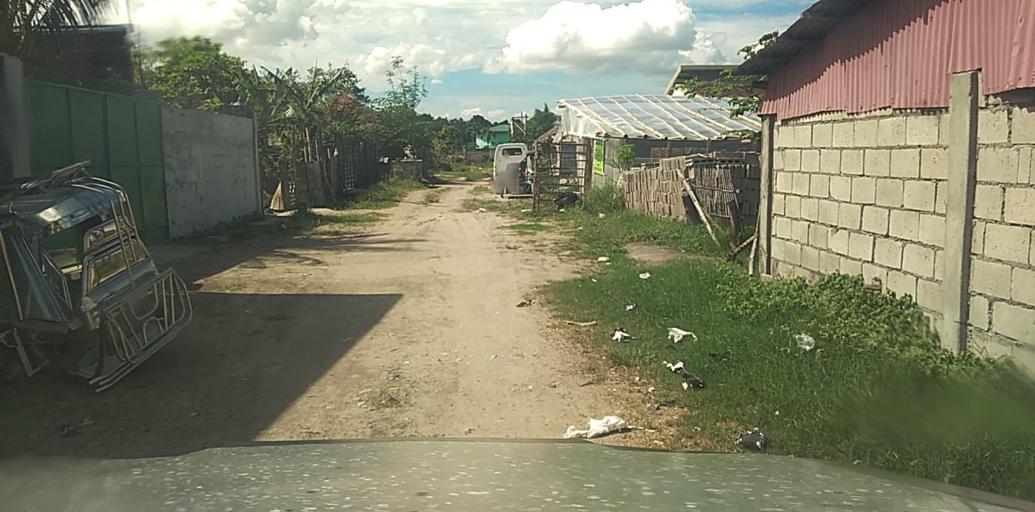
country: PH
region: Central Luzon
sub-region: Province of Pampanga
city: Buensuseso
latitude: 15.1933
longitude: 120.6673
